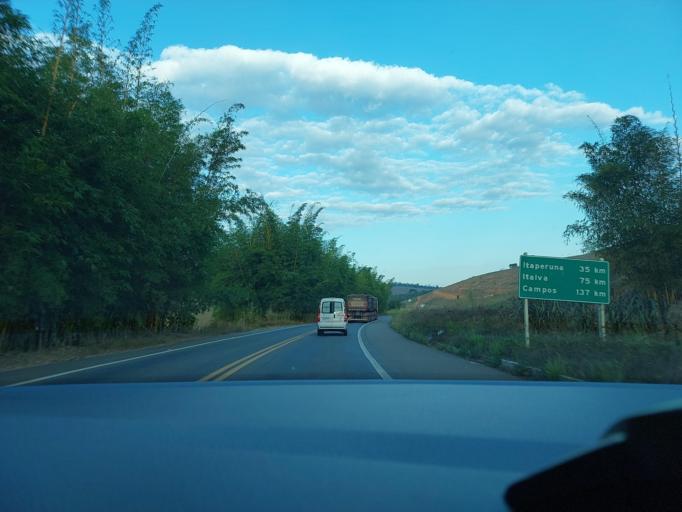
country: BR
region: Minas Gerais
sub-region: Muriae
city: Muriae
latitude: -21.1385
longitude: -42.1754
